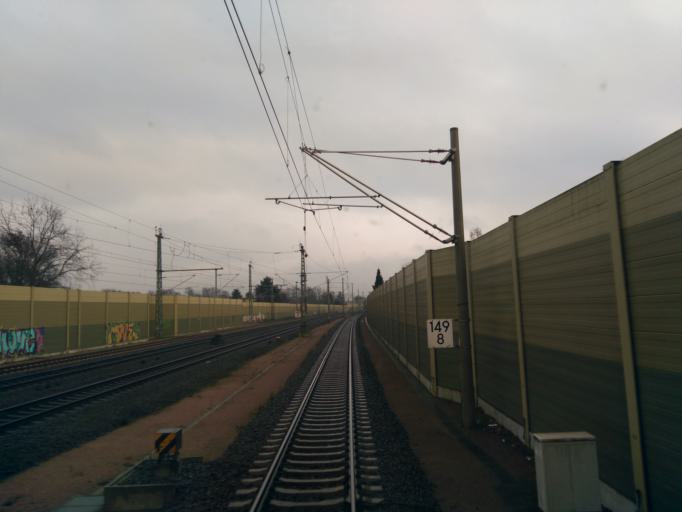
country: DE
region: Lower Saxony
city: Winsen
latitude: 53.3505
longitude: 10.2160
